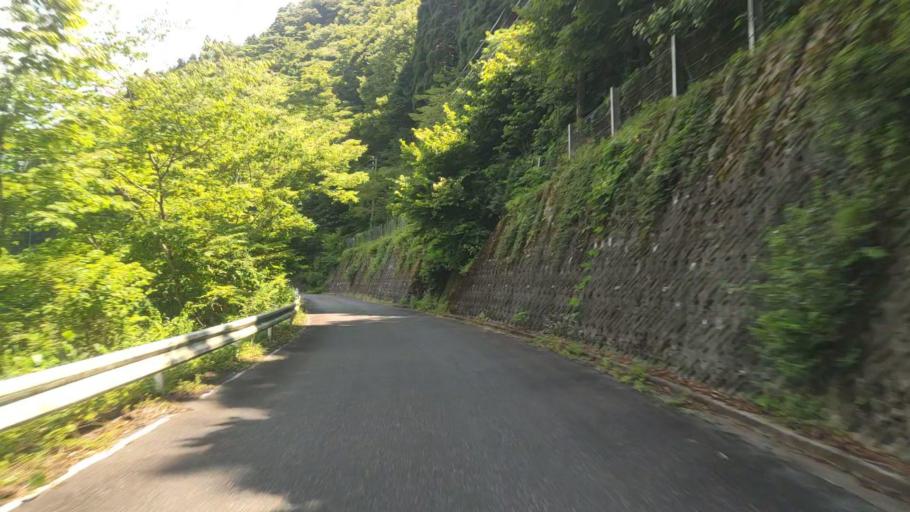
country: JP
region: Gifu
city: Godo
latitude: 35.7047
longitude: 136.5875
